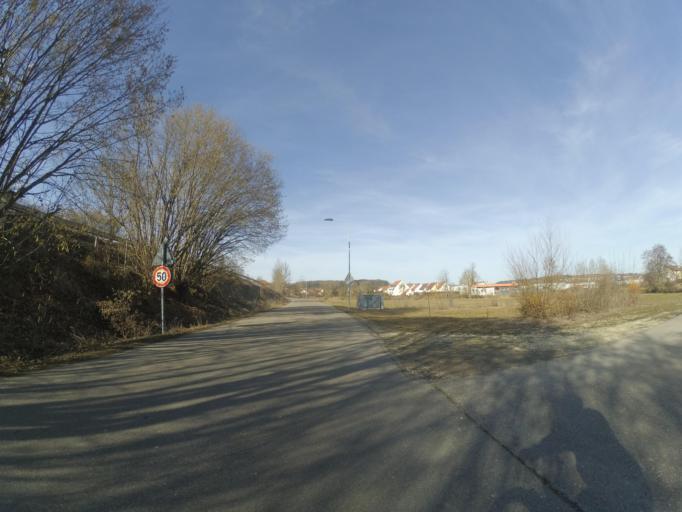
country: DE
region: Baden-Wuerttemberg
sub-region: Regierungsbezirk Stuttgart
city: Giengen an der Brenz
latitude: 48.6141
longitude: 10.2493
